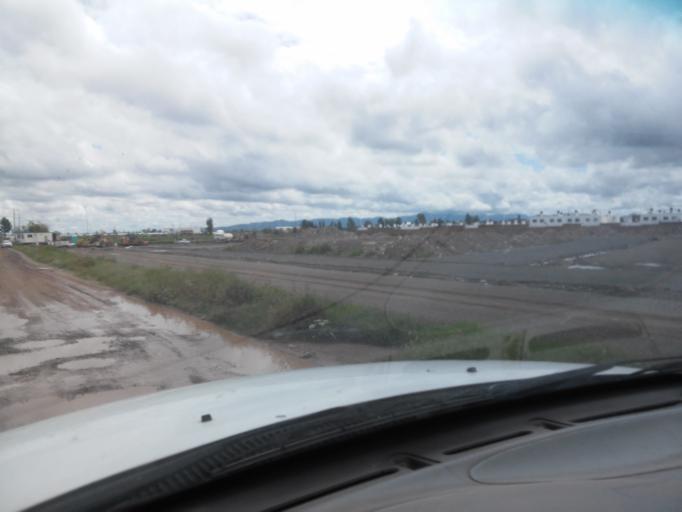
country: MX
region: Durango
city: Victoria de Durango
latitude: 24.0253
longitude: -104.6154
